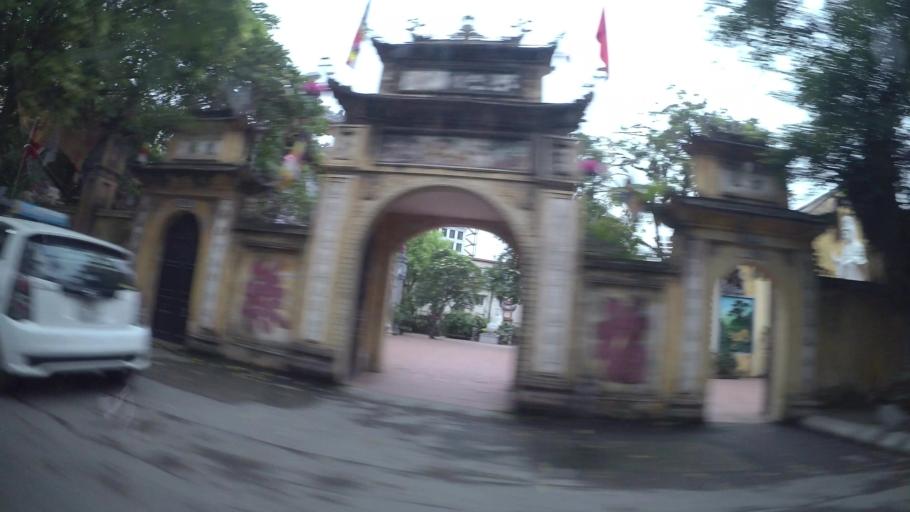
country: VN
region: Ha Noi
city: Hai BaTrung
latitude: 20.9887
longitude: 105.8776
